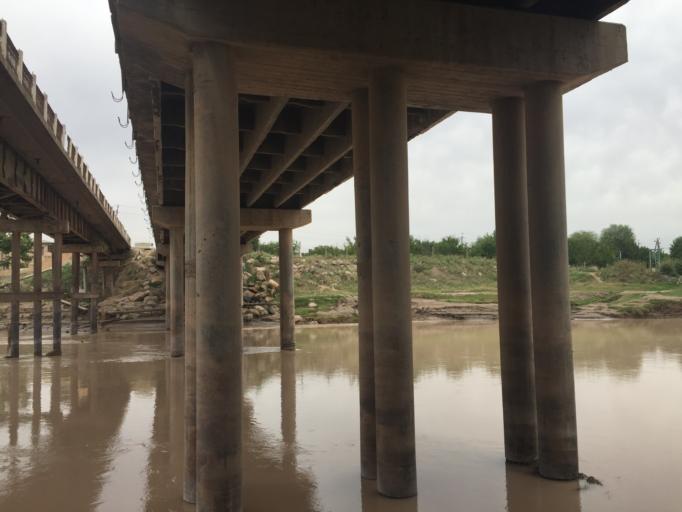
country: TJ
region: Khatlon
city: Vose'
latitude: 37.8015
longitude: 69.6492
